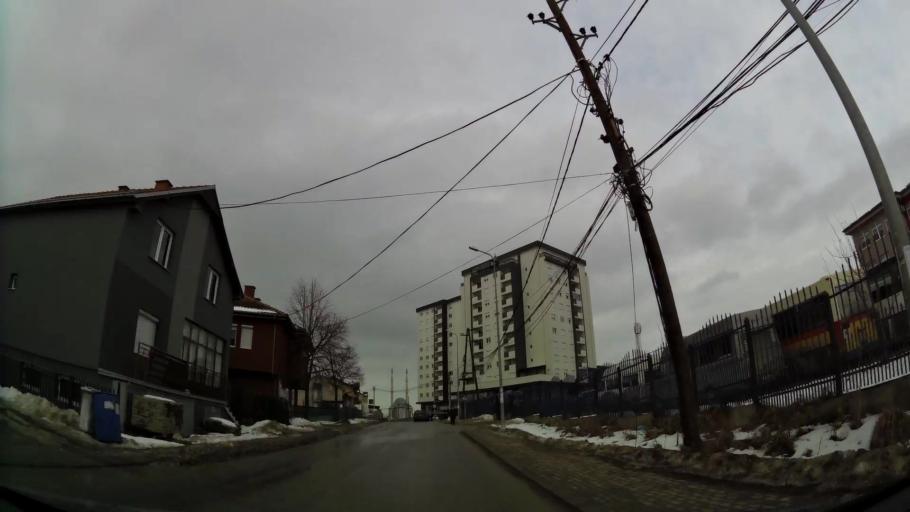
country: XK
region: Pristina
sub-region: Komuna e Prishtines
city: Pristina
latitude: 42.6538
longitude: 21.1911
